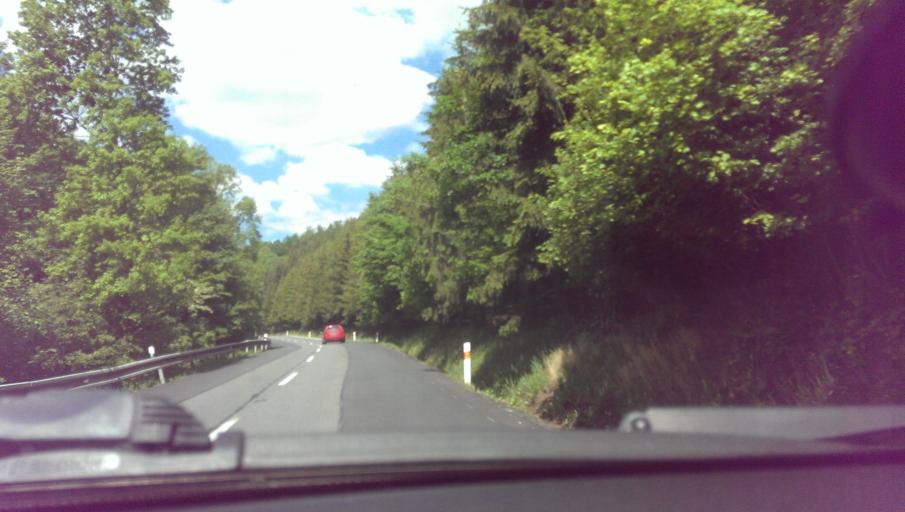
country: CZ
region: Zlin
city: Valasska Polanka
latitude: 49.2430
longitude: 17.9725
